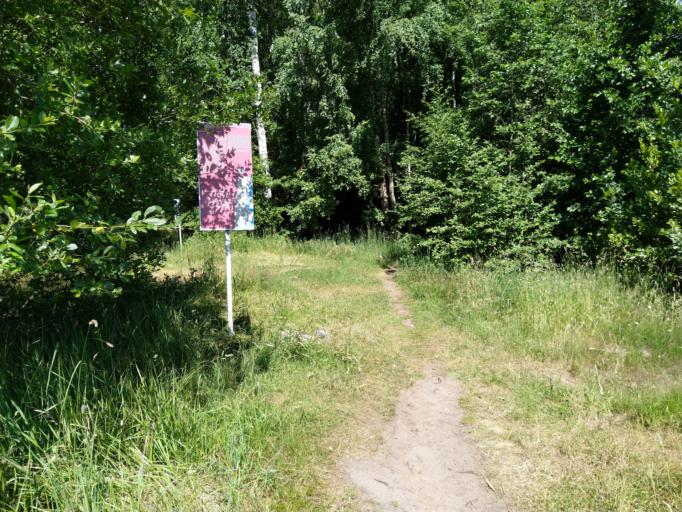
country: RU
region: Leningrad
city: Sapernoye
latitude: 60.6767
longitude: 30.0034
